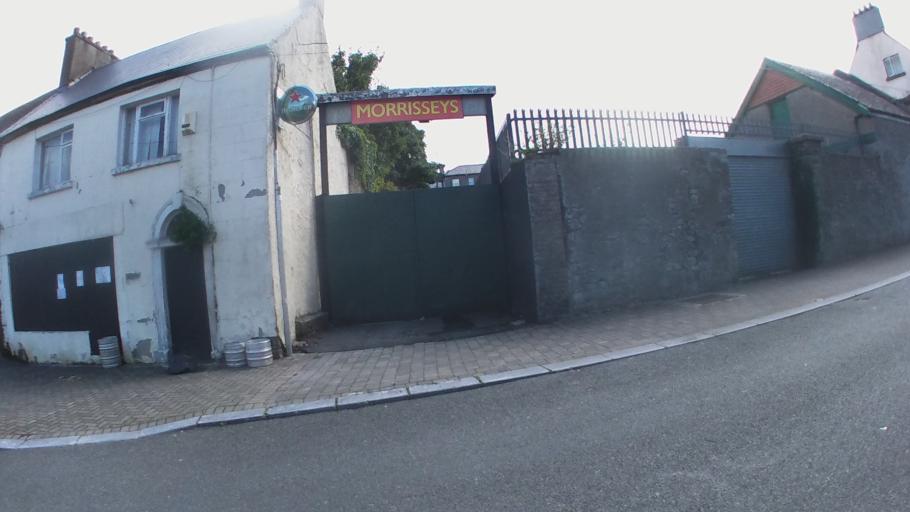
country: IE
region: Leinster
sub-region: County Carlow
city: Carlow
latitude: 52.8372
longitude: -6.9329
